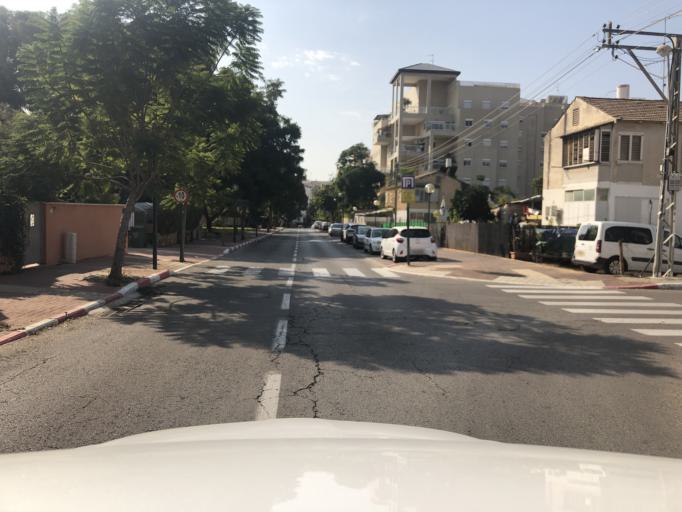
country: IL
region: Central District
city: Kfar Saba
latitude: 32.1811
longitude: 34.9068
